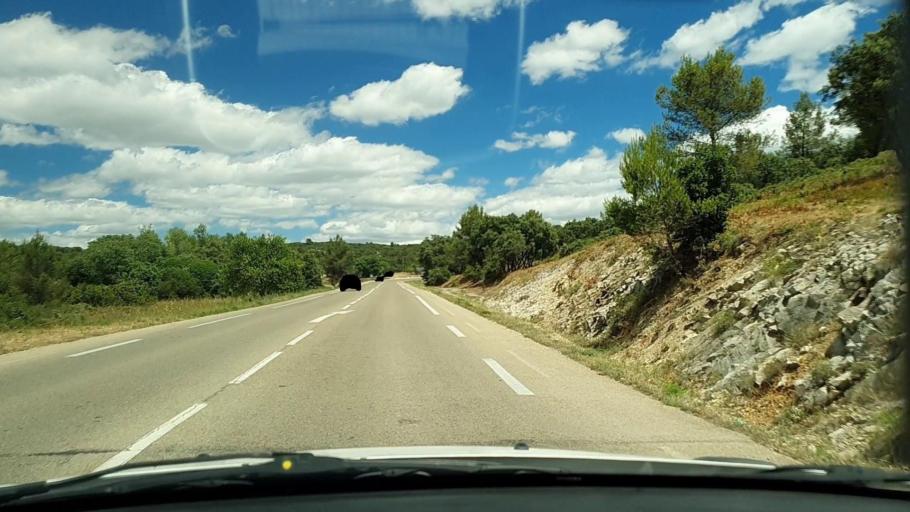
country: FR
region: Languedoc-Roussillon
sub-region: Departement du Gard
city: Poulx
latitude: 43.8892
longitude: 4.4168
